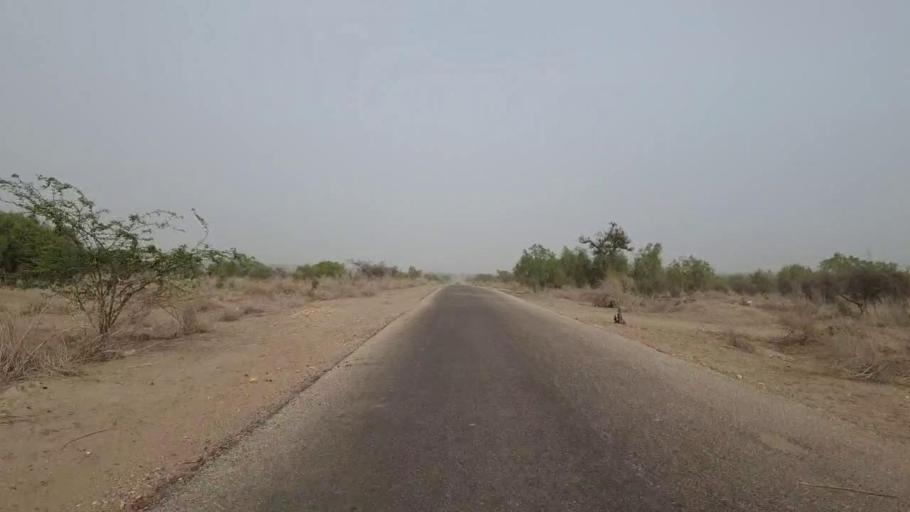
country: PK
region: Sindh
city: Islamkot
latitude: 24.5689
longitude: 70.3252
